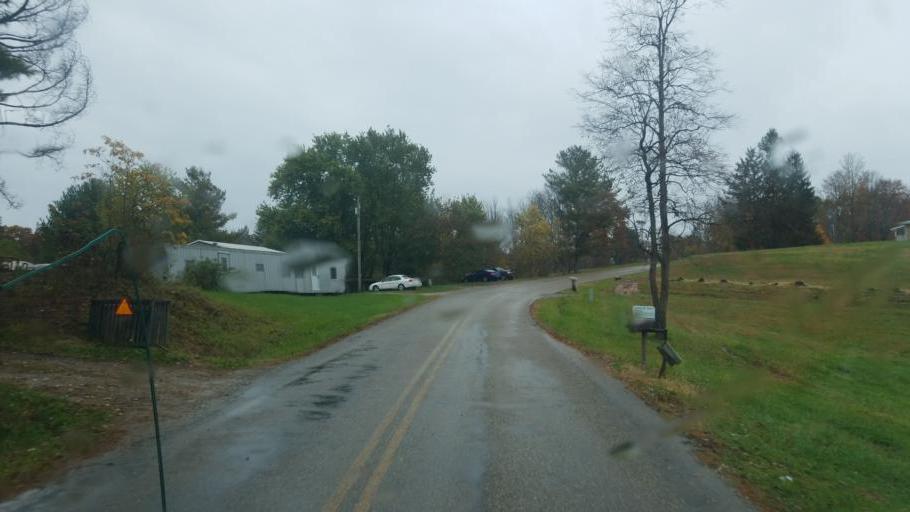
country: US
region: West Virginia
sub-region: Wood County
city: Blennerhassett
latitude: 39.3419
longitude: -81.6283
